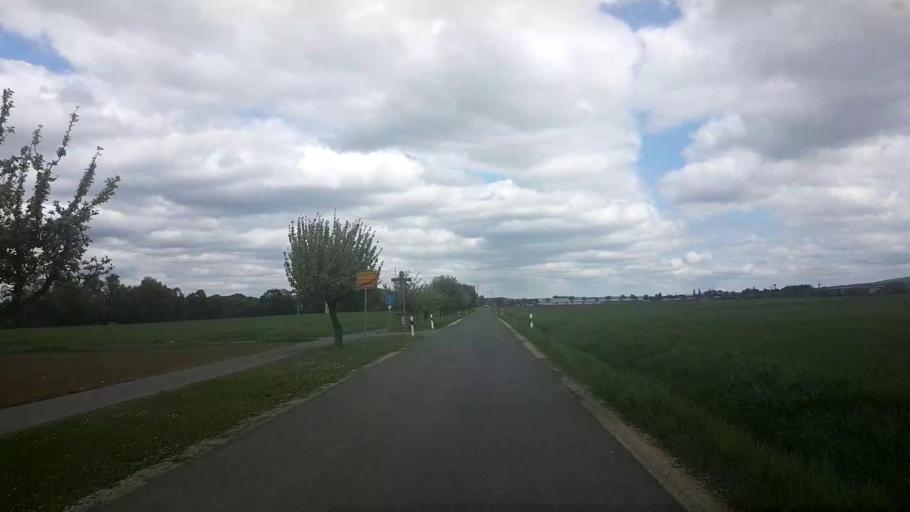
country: DE
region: Bavaria
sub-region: Upper Franconia
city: Bad Staffelstein
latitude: 50.1214
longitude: 11.0139
